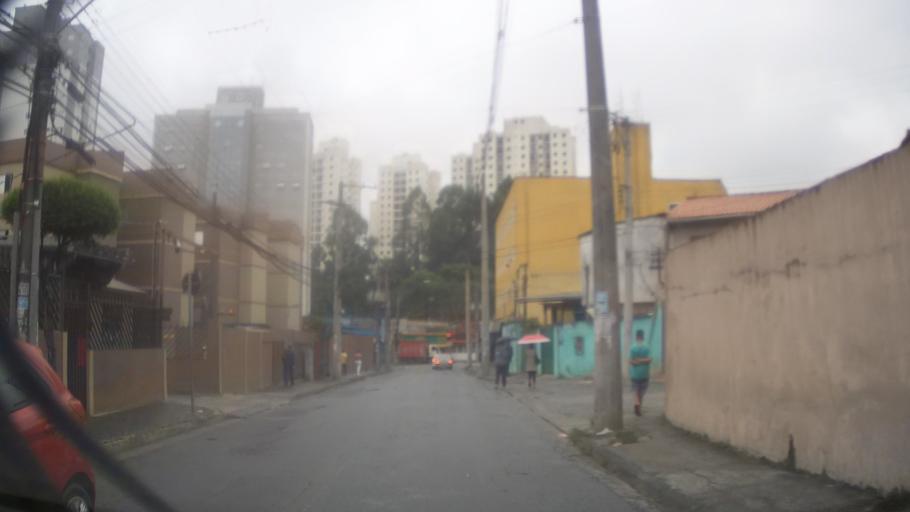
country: BR
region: Sao Paulo
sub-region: Guarulhos
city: Guarulhos
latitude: -23.4417
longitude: -46.5350
